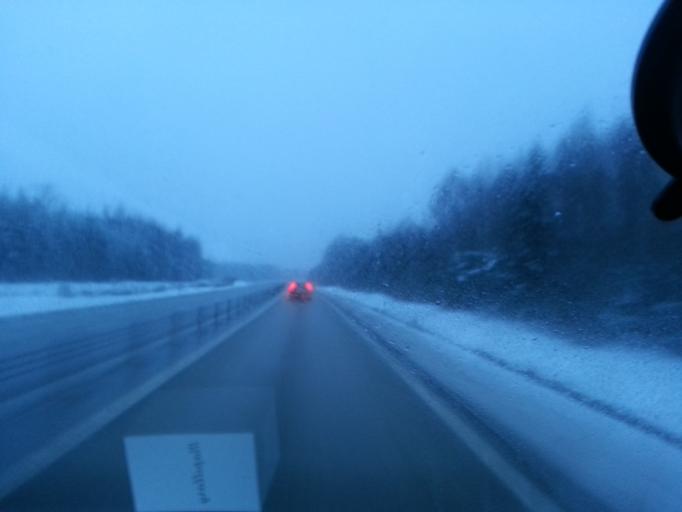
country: SE
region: Kronoberg
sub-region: Ljungby Kommun
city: Lagan
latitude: 57.0100
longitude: 14.0386
